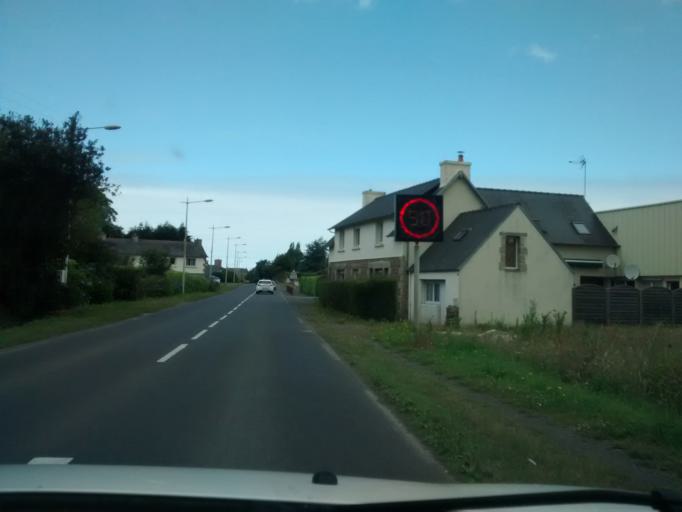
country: FR
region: Brittany
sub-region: Departement des Cotes-d'Armor
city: Louannec
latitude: 48.7915
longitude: -3.4042
